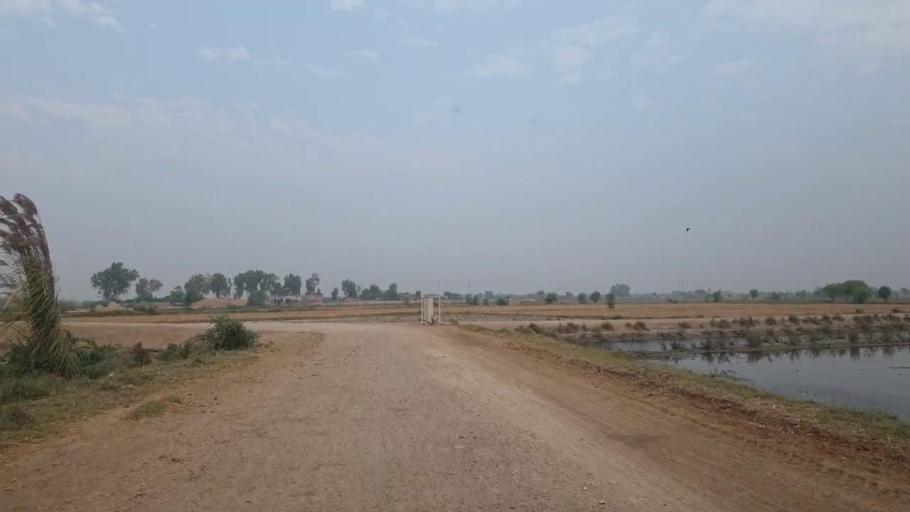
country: PK
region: Sindh
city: Tando Bago
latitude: 24.7892
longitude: 68.8852
